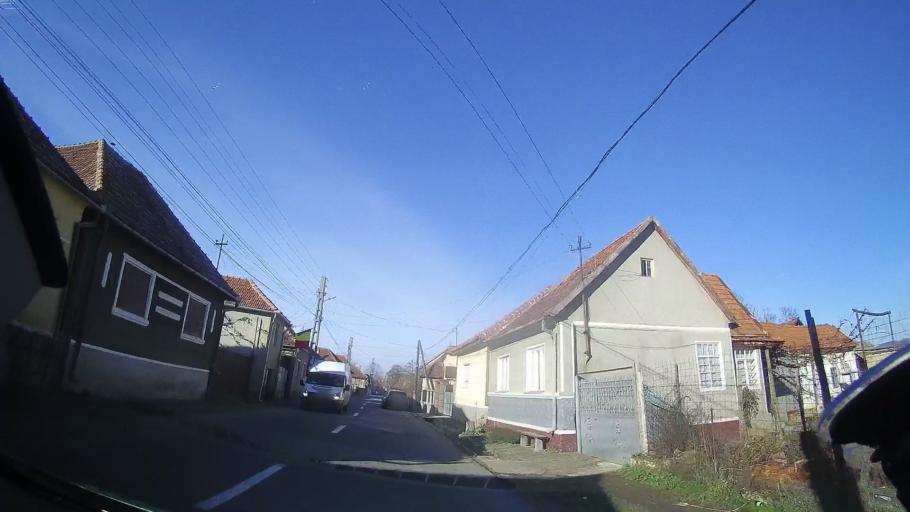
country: RO
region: Bihor
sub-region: Comuna Vadu Crisului
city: Vadu Crisului
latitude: 46.9885
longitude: 22.5118
